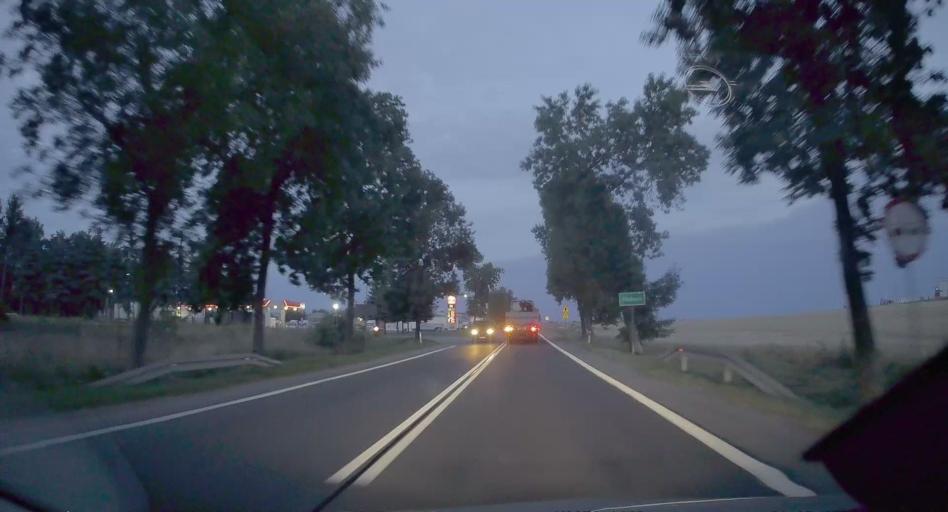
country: PL
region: Silesian Voivodeship
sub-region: Powiat klobucki
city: Klobuck
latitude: 50.9131
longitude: 18.9000
